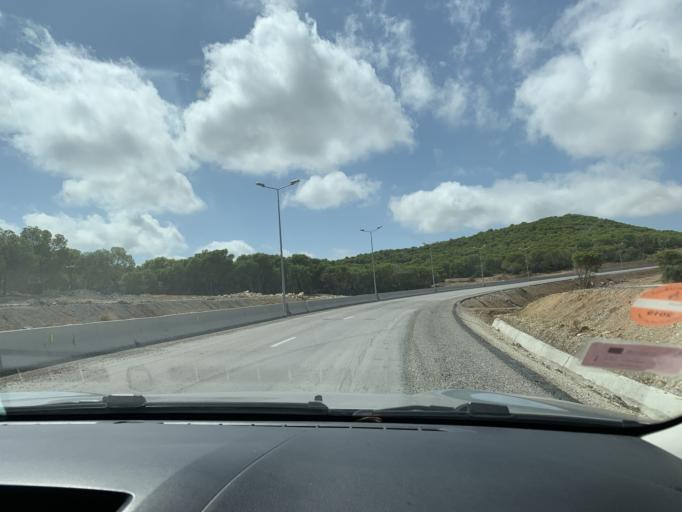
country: TN
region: Zaghwan
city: El Fahs
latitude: 36.2742
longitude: 9.8060
